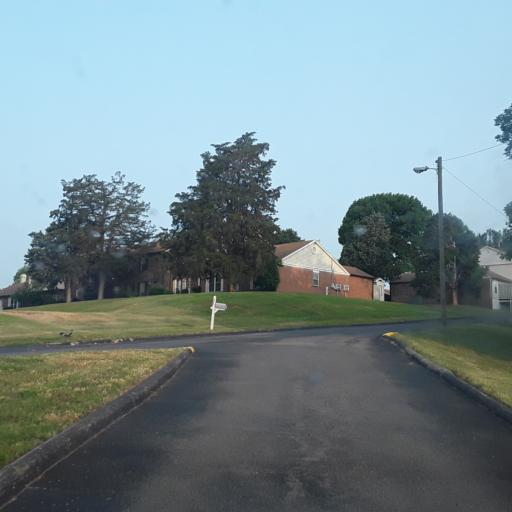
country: US
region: Tennessee
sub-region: Williamson County
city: Brentwood Estates
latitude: 36.0488
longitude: -86.7254
